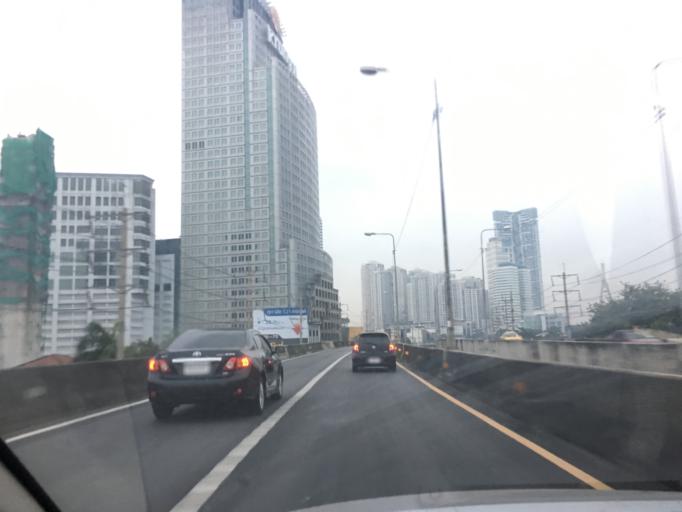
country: TH
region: Bangkok
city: Yan Nawa
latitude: 13.6792
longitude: 100.5473
